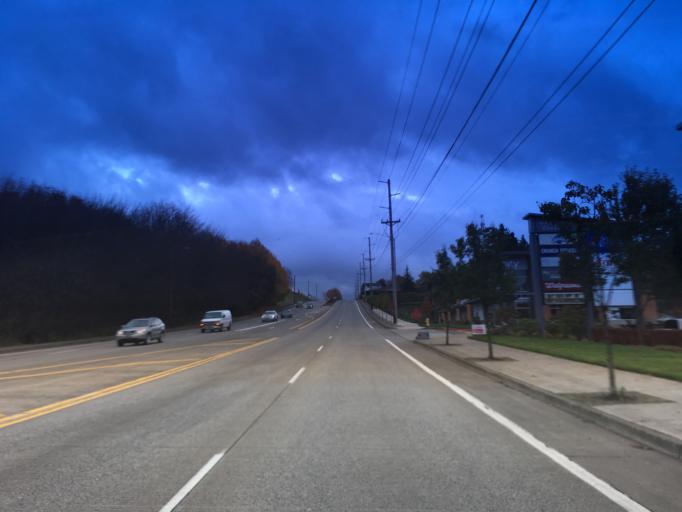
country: US
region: Oregon
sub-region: Multnomah County
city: Fairview
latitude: 45.5264
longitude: -122.4338
